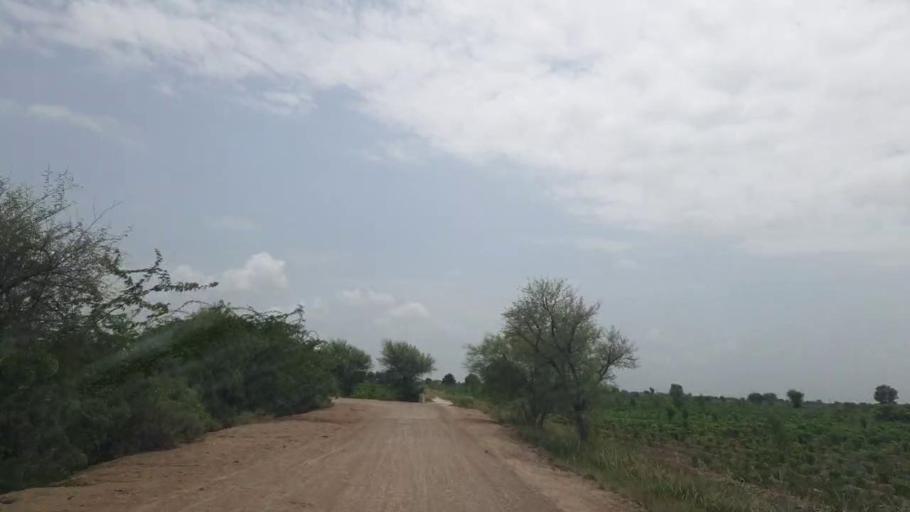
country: PK
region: Sindh
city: Naukot
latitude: 24.9040
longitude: 69.2009
